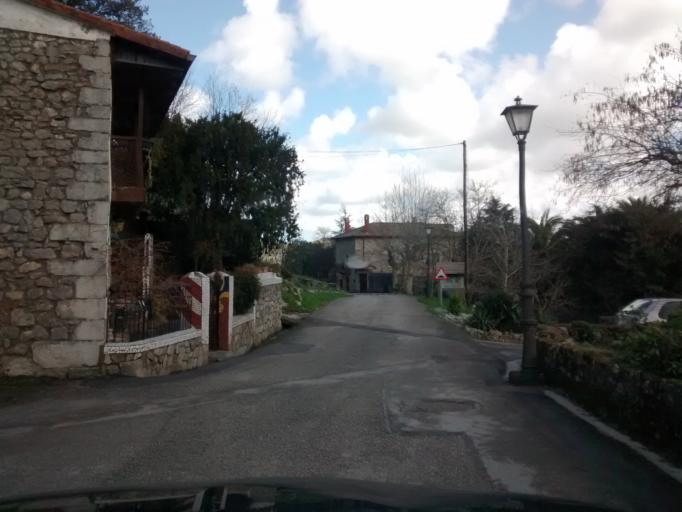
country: ES
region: Cantabria
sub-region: Provincia de Cantabria
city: Lierganes
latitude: 43.3421
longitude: -3.7207
